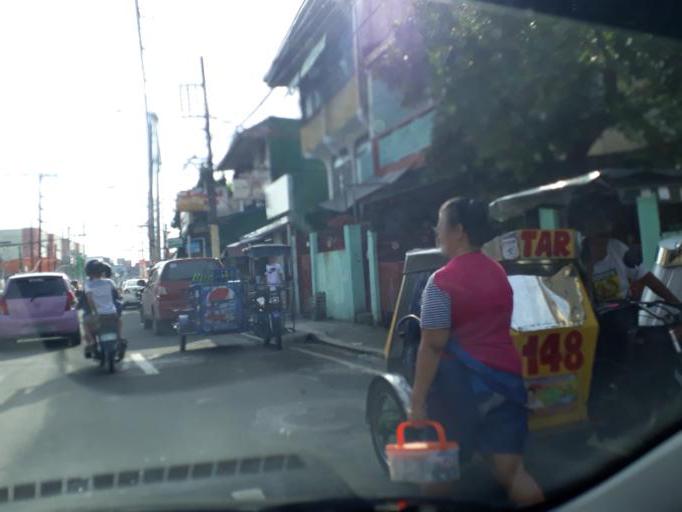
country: PH
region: Metro Manila
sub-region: Caloocan City
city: Niugan
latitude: 14.6516
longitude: 120.9760
